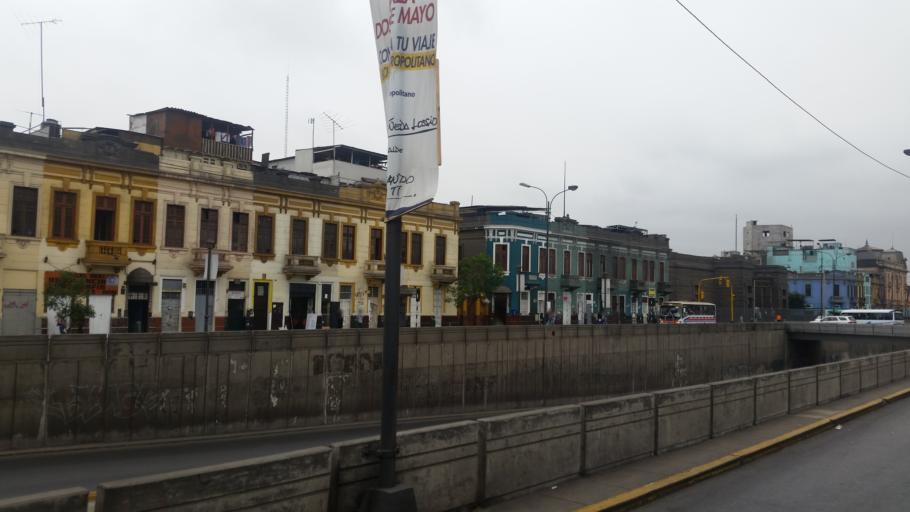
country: PE
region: Lima
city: Lima
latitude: -12.0490
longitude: -77.0424
